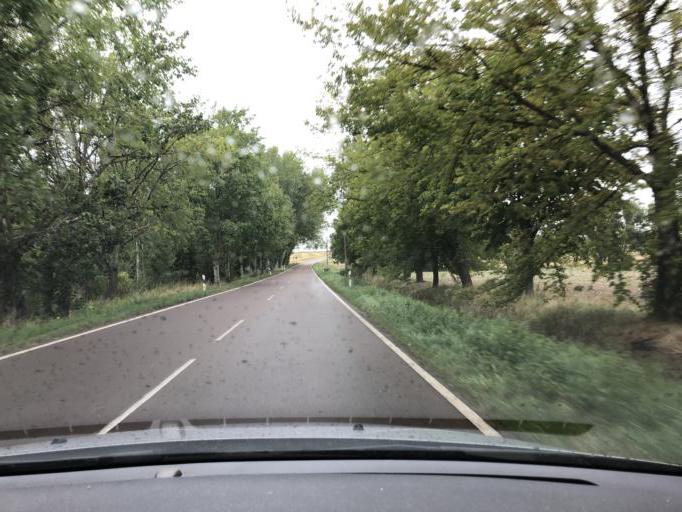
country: DE
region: Saxony-Anhalt
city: Wulfen
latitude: 51.8188
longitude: 11.9063
